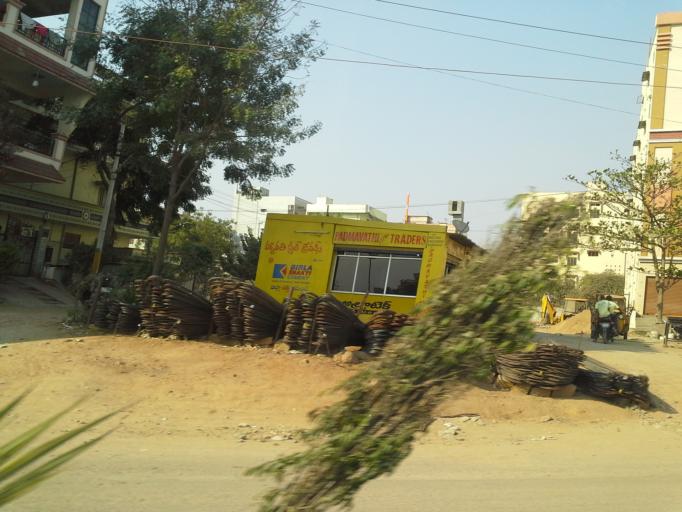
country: IN
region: Telangana
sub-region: Rangareddi
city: Balapur
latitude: 17.2599
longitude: 78.3845
